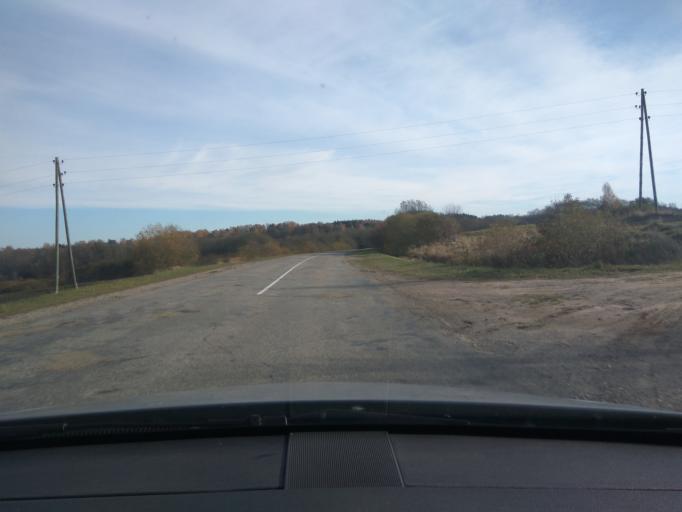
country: LV
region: Alsunga
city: Alsunga
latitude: 57.0062
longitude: 21.7329
